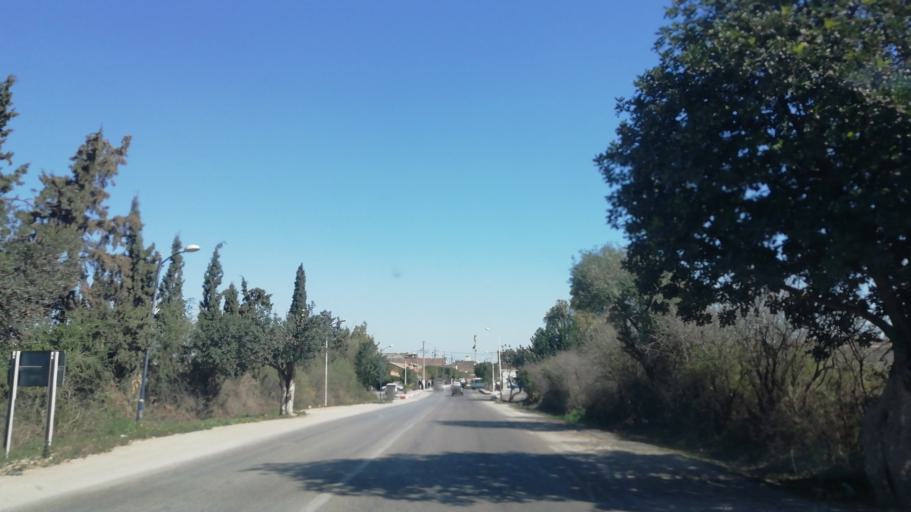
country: DZ
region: Mascara
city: Sig
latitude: 35.5618
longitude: -0.0934
